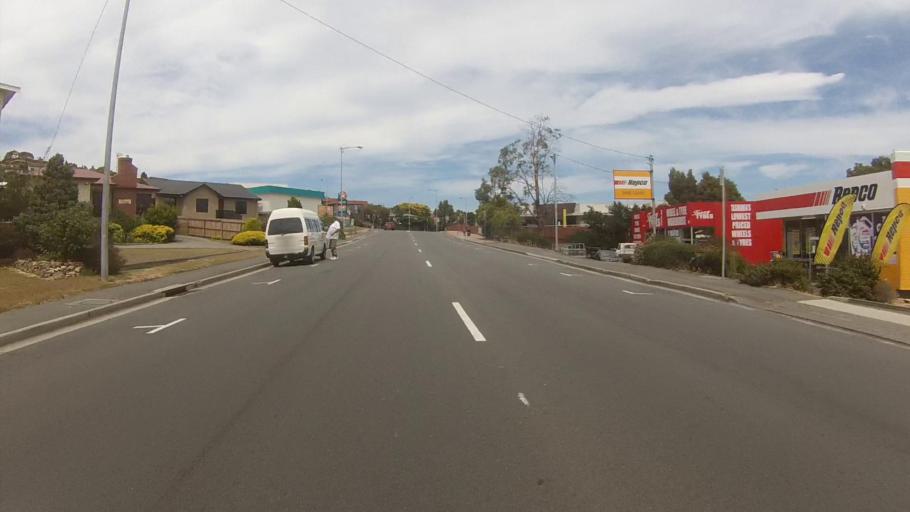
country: AU
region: Tasmania
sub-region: Clarence
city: Bellerive
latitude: -42.8651
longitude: 147.3722
